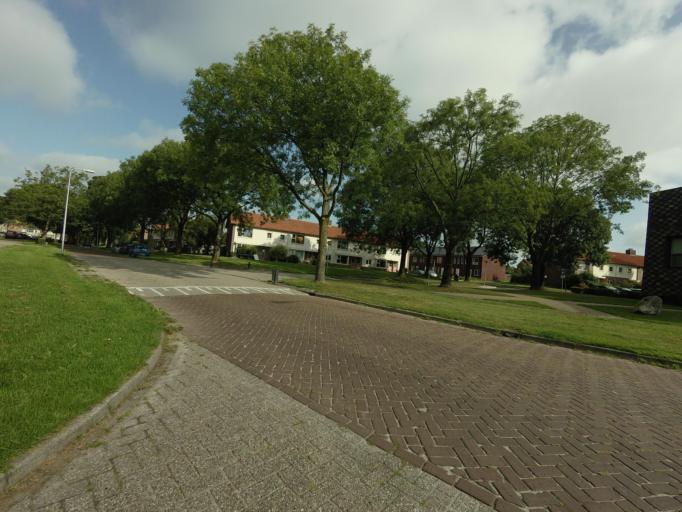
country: NL
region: Overijssel
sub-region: Gemeente Steenwijkerland
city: Steenwijk
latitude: 52.7818
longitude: 6.1048
